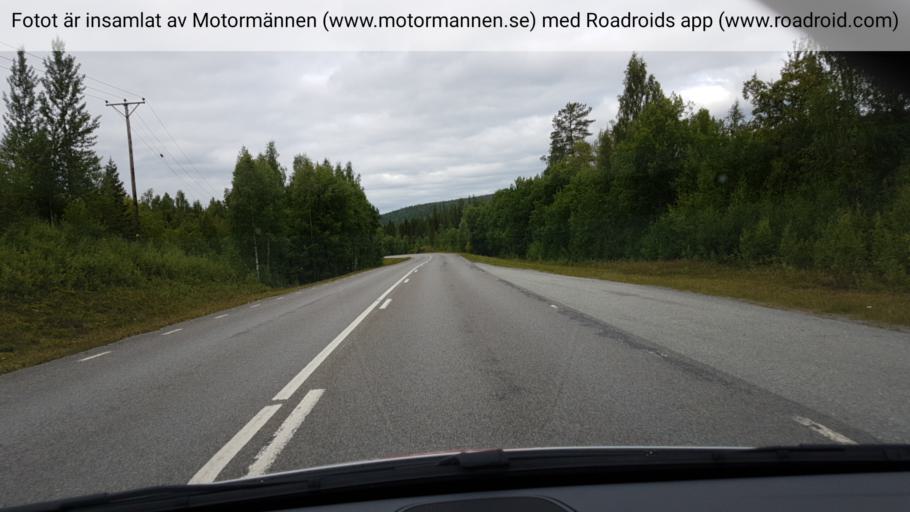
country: SE
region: Jaemtland
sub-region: Stroemsunds Kommun
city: Stroemsund
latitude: 64.3128
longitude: 15.2153
